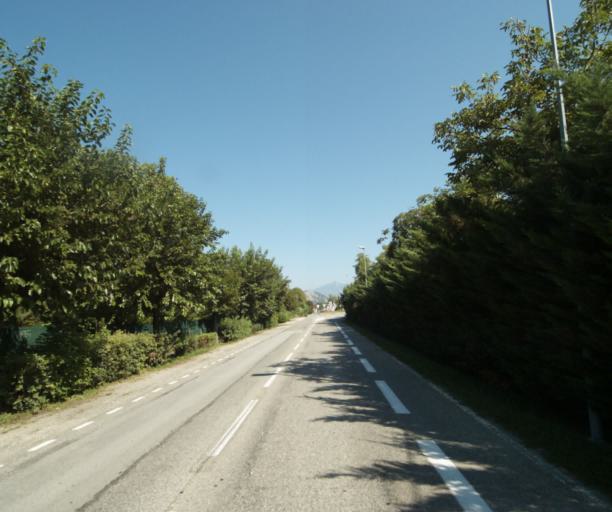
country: FR
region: Rhone-Alpes
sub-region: Departement de l'Isere
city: Allieres-et-Risset
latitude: 45.0923
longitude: 5.6837
